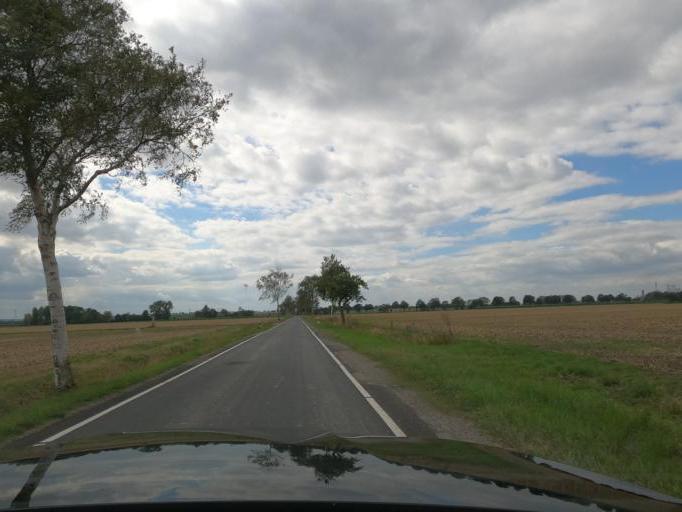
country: DE
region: Lower Saxony
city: Hohenhameln
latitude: 52.2264
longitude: 10.0736
